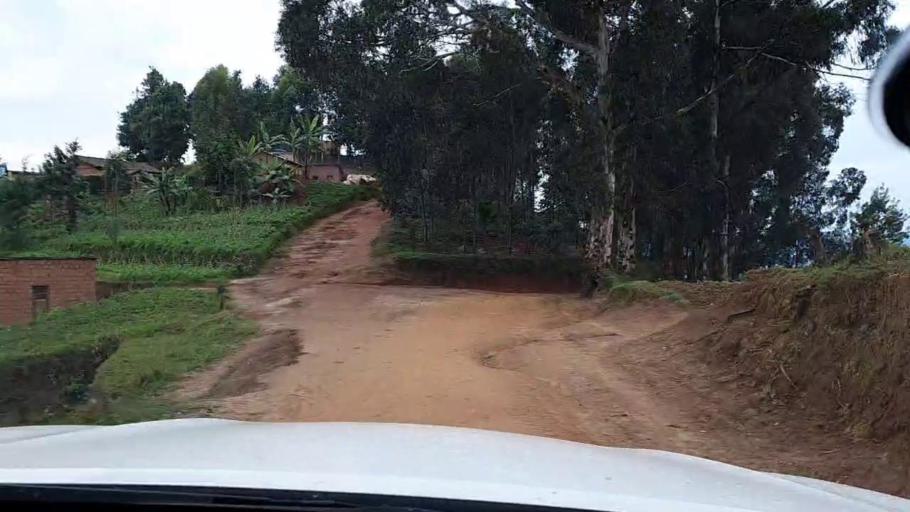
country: RW
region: Southern Province
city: Nzega
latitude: -2.3788
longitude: 29.2434
